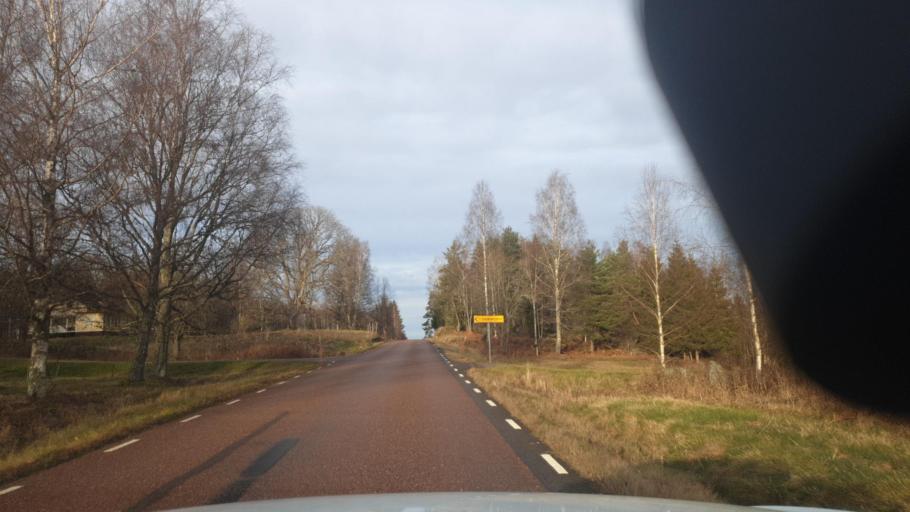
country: NO
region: Ostfold
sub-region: Romskog
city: Romskog
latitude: 59.7150
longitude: 12.0693
